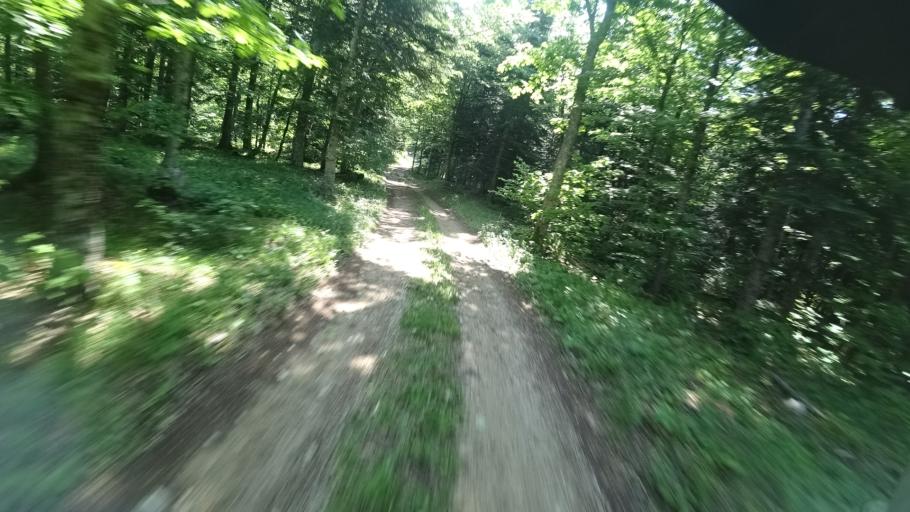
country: BA
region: Federation of Bosnia and Herzegovina
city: Izacic
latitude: 44.7605
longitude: 15.7523
